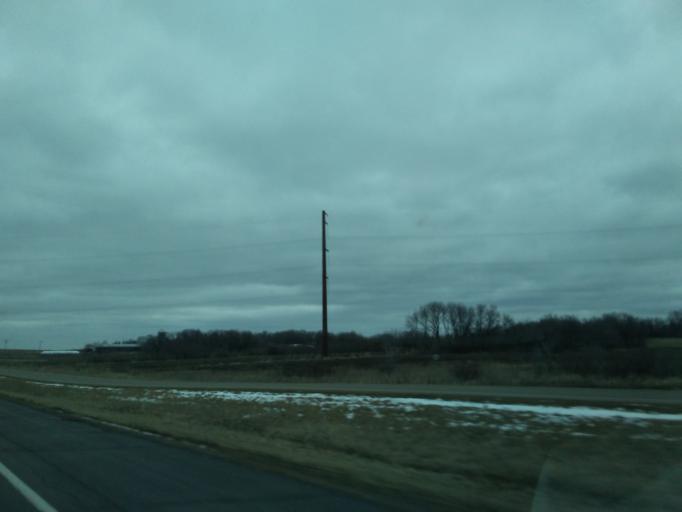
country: US
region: Minnesota
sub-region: Goodhue County
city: Cannon Falls
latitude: 44.6113
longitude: -92.9945
